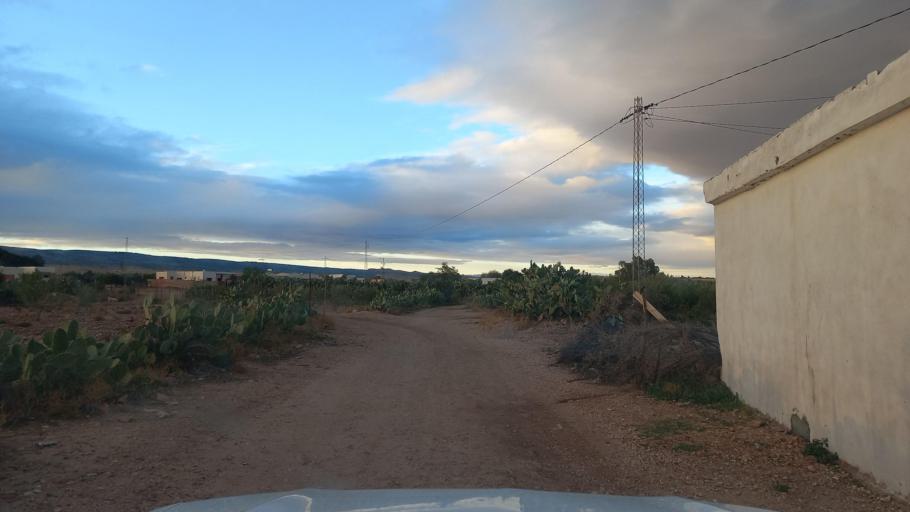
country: TN
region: Al Qasrayn
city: Kasserine
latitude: 35.2585
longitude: 8.9425
